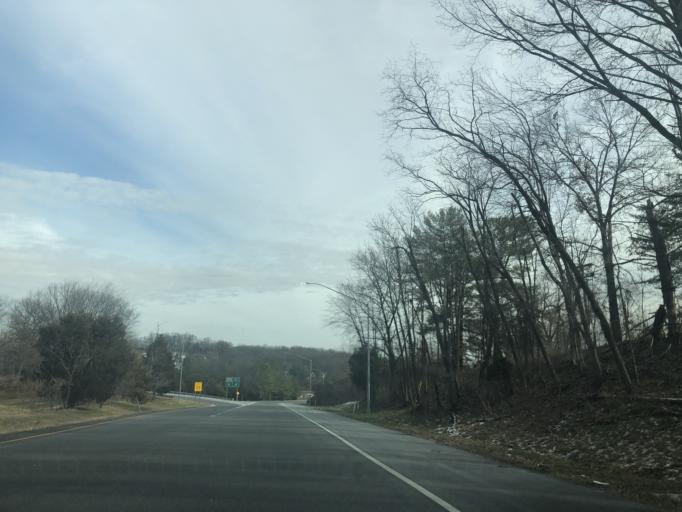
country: US
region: Maryland
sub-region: Howard County
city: Elkridge
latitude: 39.2326
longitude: -76.7106
